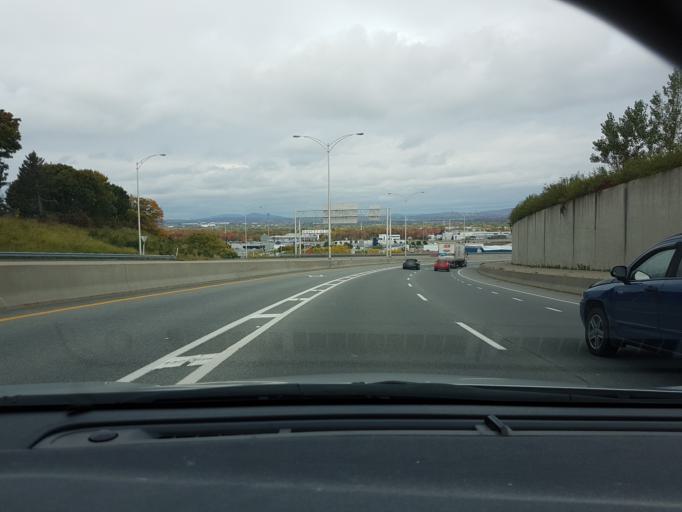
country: CA
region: Quebec
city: L'Ancienne-Lorette
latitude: 46.7872
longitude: -71.2905
